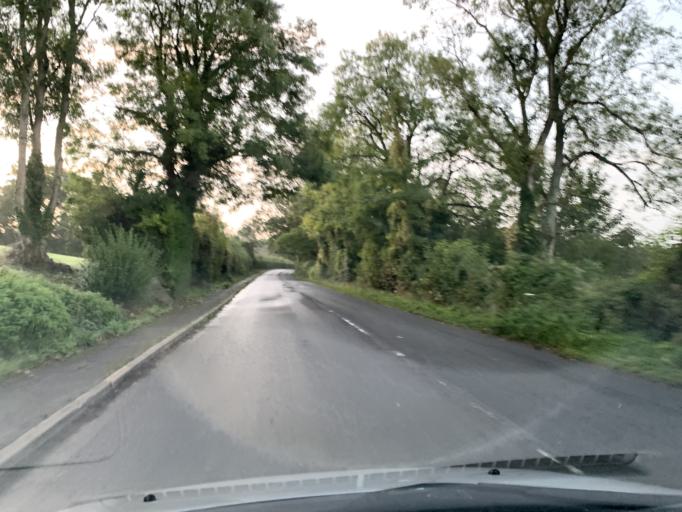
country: GB
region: England
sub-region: Wiltshire
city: Alderbury
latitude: 51.0517
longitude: -1.7520
